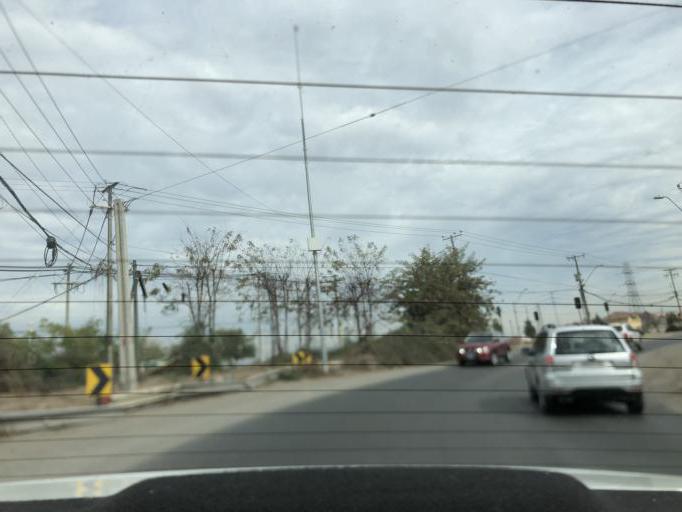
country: CL
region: Santiago Metropolitan
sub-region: Provincia de Cordillera
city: Puente Alto
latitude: -33.6114
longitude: -70.5427
